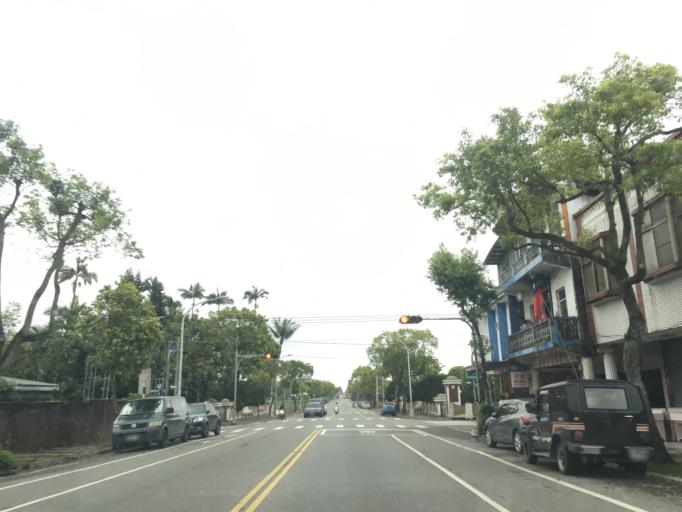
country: TW
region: Taiwan
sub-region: Hualien
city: Hualian
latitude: 23.9741
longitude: 121.5637
